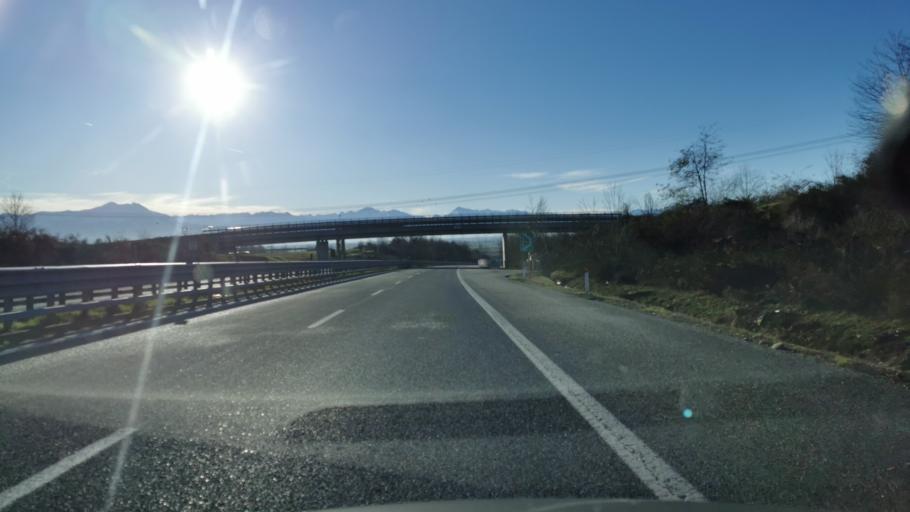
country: IT
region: Piedmont
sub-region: Provincia di Cuneo
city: Magliano Alpi
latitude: 44.4716
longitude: 7.7851
